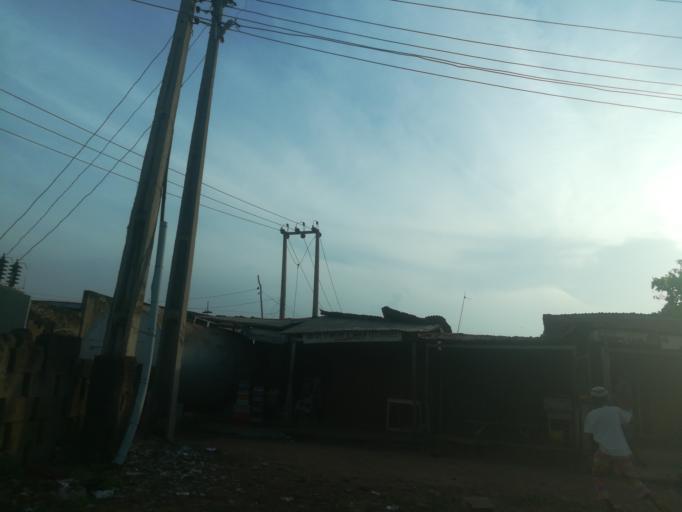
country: NG
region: Oyo
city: Moniya
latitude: 7.5356
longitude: 3.9039
